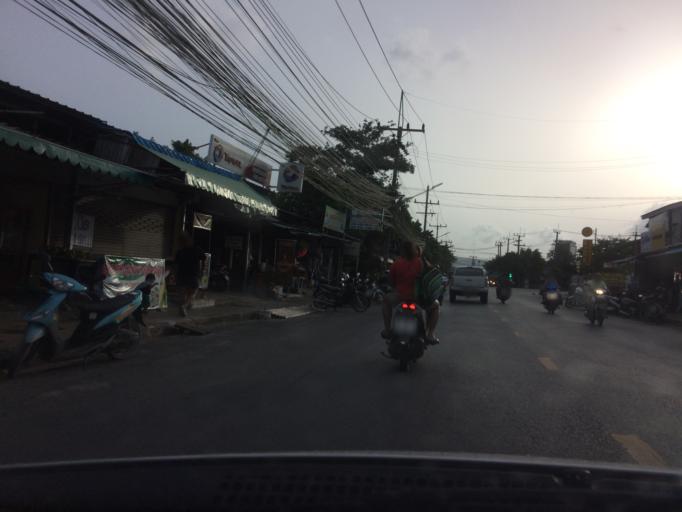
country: TH
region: Phuket
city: Ban Talat Yai
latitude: 7.8813
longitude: 98.4015
